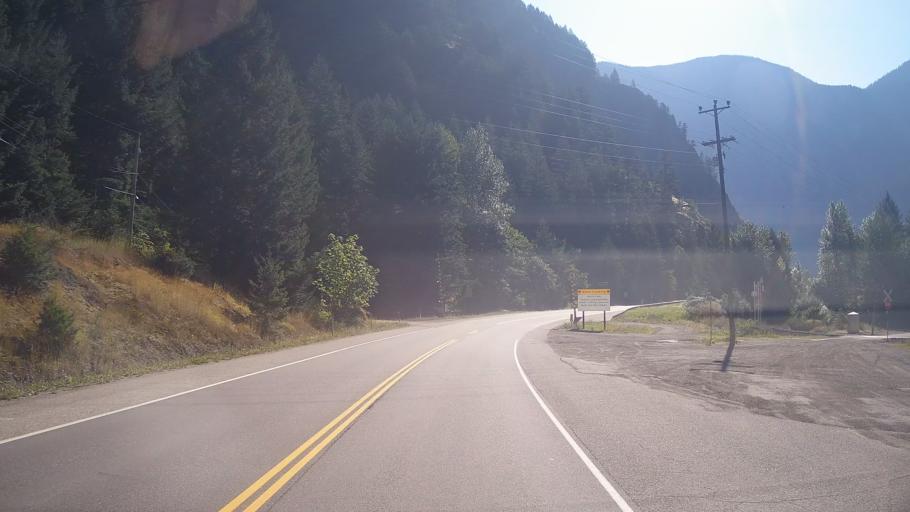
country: CA
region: British Columbia
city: Hope
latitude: 49.5636
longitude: -121.4250
